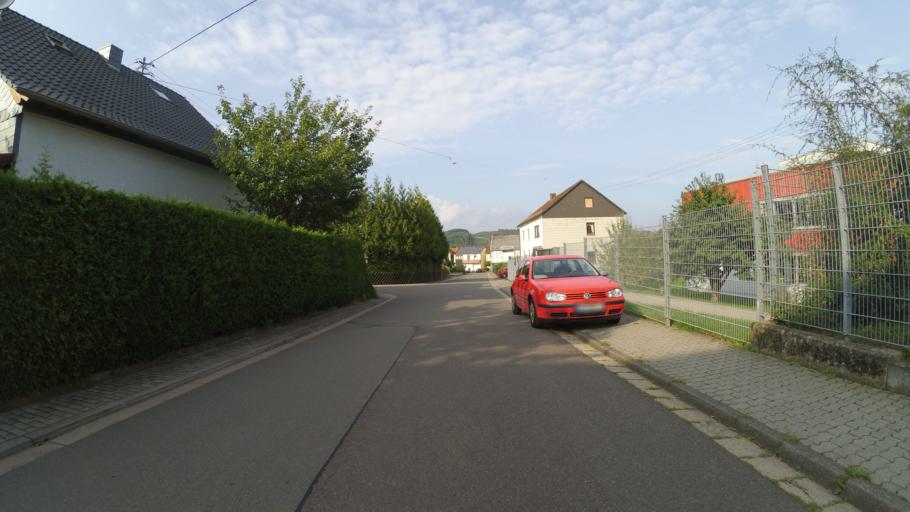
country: DE
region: Saarland
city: Weiskirchen
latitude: 49.5560
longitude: 6.8160
